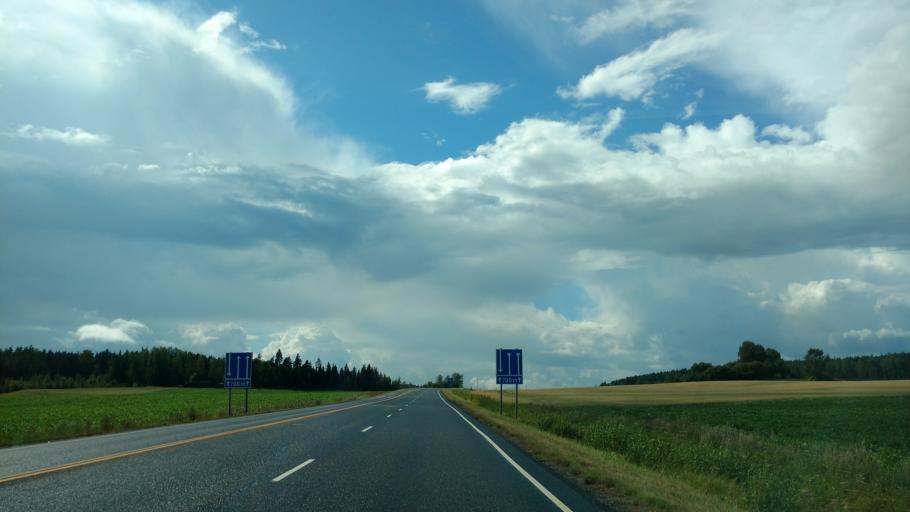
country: FI
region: Varsinais-Suomi
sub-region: Salo
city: Halikko
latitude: 60.3758
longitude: 22.9776
